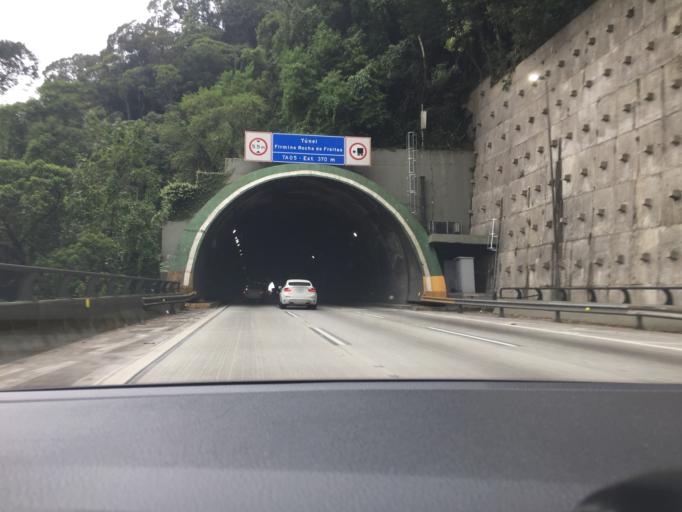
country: BR
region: Sao Paulo
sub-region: Cubatao
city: Cubatao
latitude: -23.9110
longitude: -46.5185
